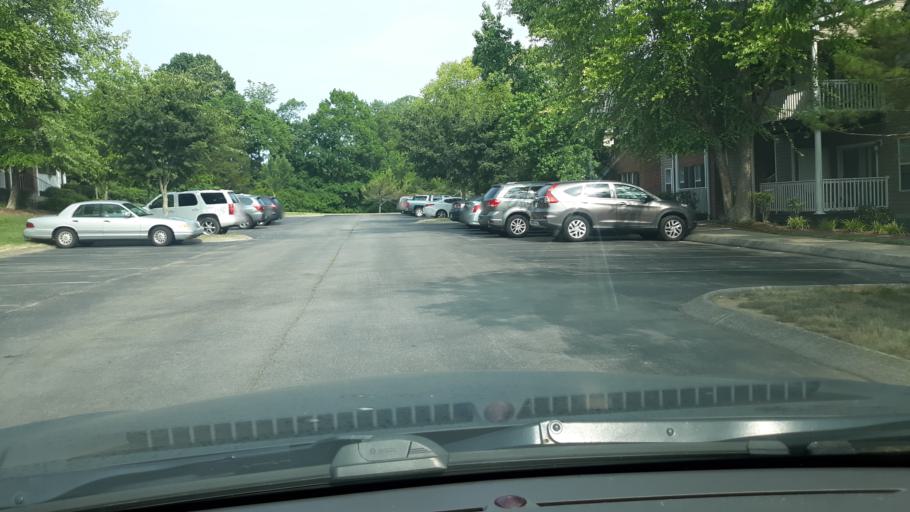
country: US
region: Tennessee
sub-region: Davidson County
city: Lakewood
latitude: 36.1838
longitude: -86.6052
